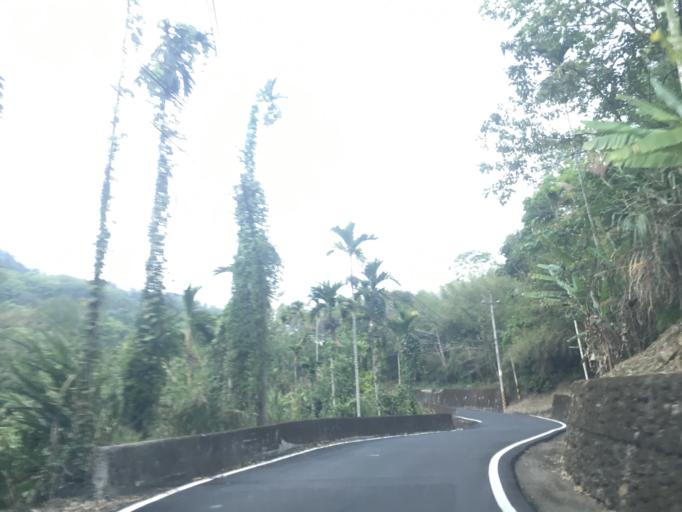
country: TW
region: Taiwan
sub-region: Nantou
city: Puli
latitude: 23.9513
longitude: 120.8652
